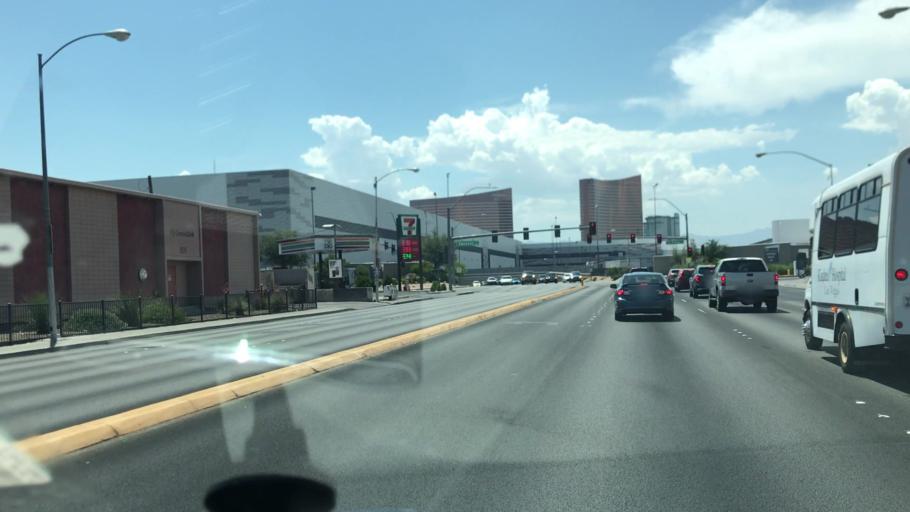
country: US
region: Nevada
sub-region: Clark County
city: Winchester
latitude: 36.1298
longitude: -115.1448
